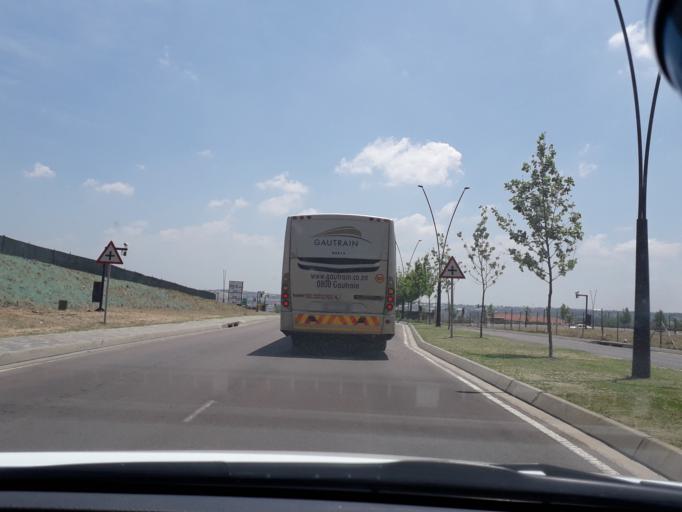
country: ZA
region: Gauteng
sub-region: City of Johannesburg Metropolitan Municipality
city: Midrand
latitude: -26.0169
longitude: 28.1048
